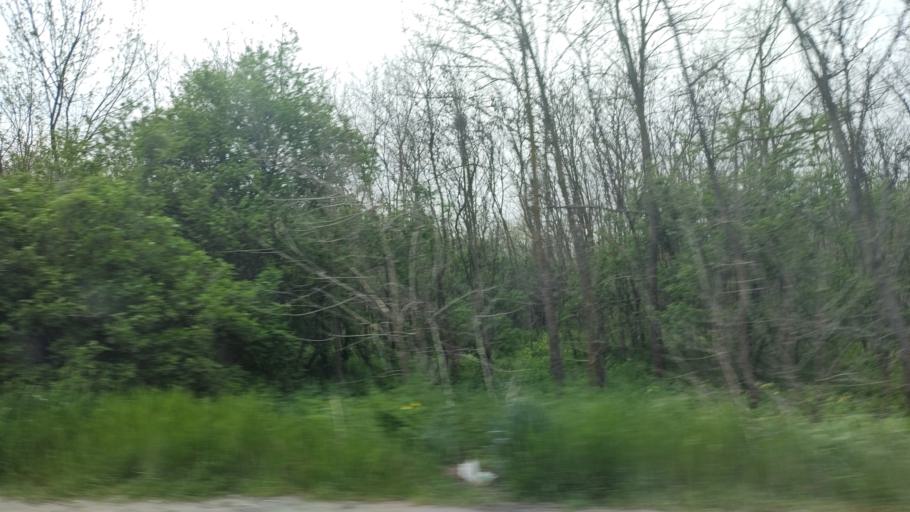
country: RO
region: Constanta
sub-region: Oras Murfatlar
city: Murfatlar
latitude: 44.1693
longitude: 28.4014
